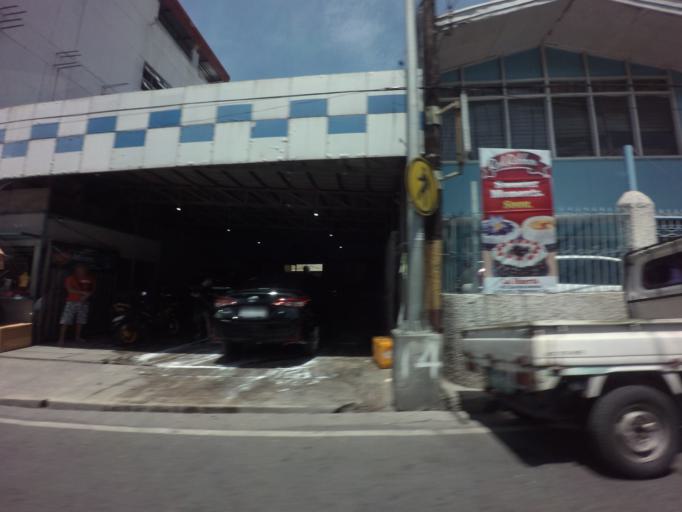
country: PH
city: Sambayanihan People's Village
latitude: 14.5027
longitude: 120.9930
